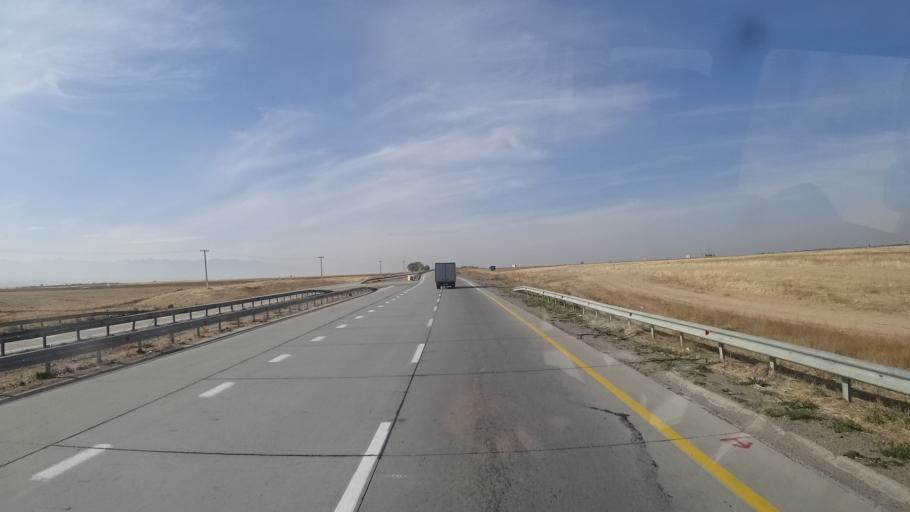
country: KZ
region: Zhambyl
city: Merke
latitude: 42.8899
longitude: 72.9801
